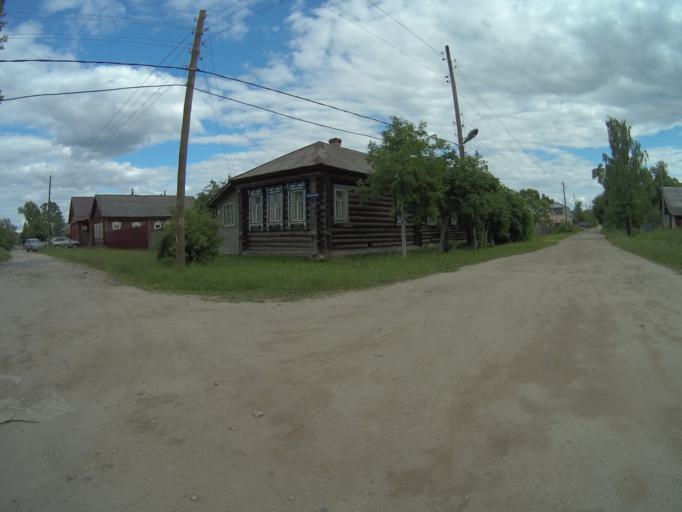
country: RU
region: Vladimir
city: Sudogda
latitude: 55.9558
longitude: 40.8572
